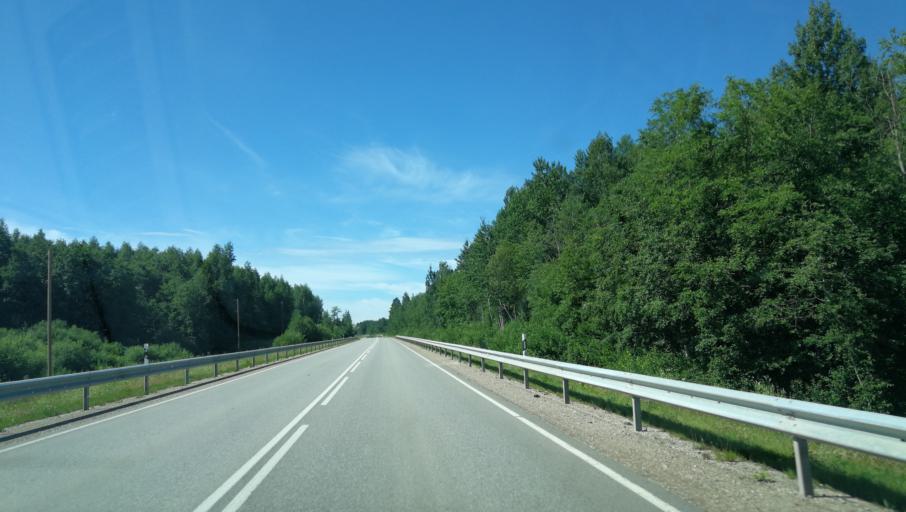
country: LV
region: Gulbenes Rajons
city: Gulbene
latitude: 57.1054
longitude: 26.6514
